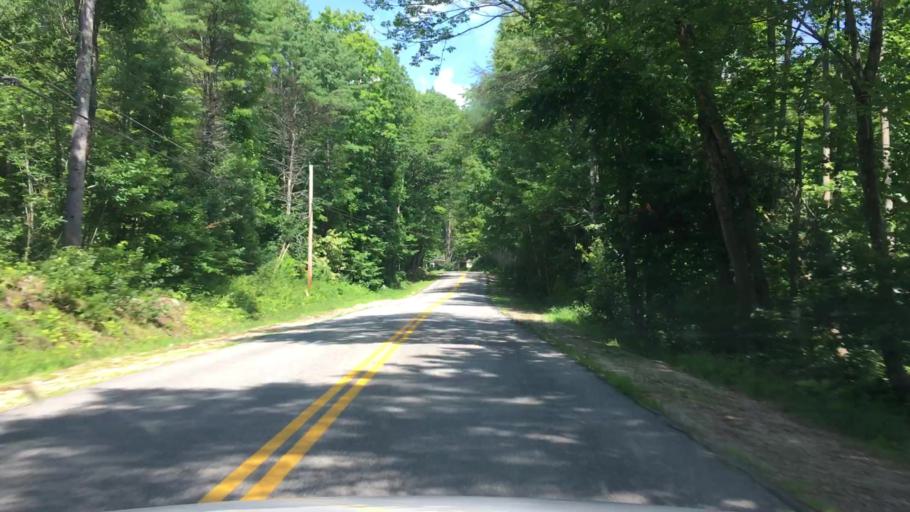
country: US
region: Maine
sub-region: Cumberland County
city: Raymond
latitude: 43.9394
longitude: -70.5227
